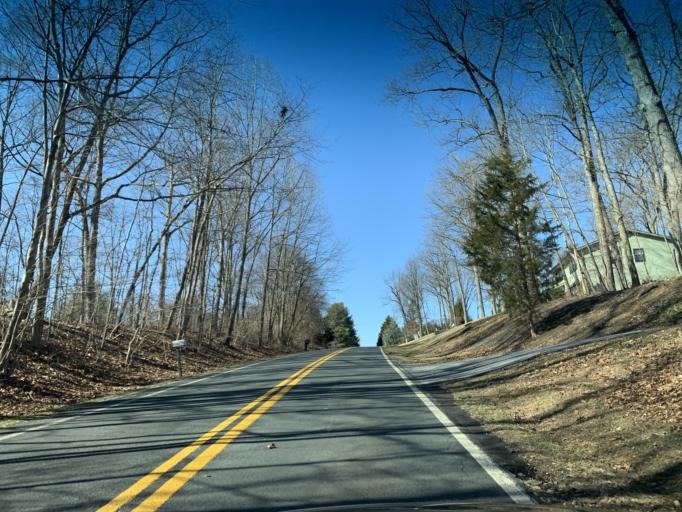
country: US
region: Maryland
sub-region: Carroll County
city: Hampstead
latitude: 39.5828
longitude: -76.9018
